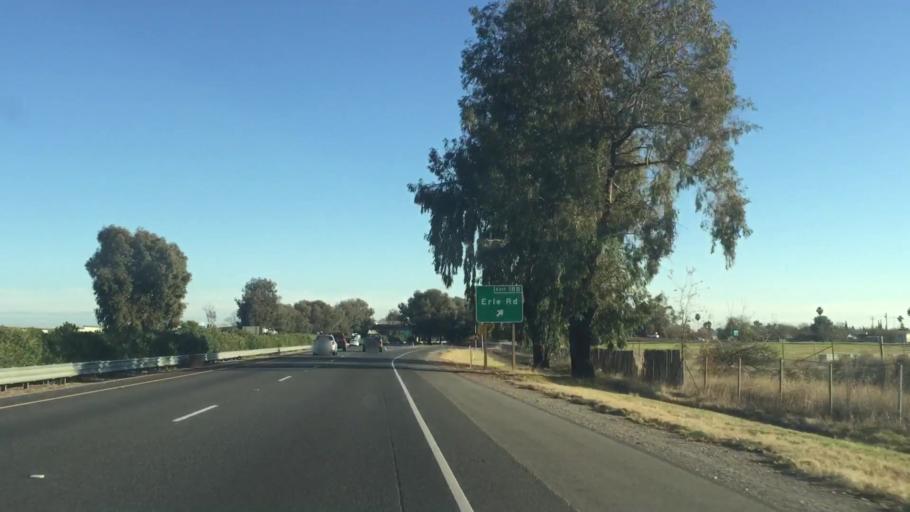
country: US
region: California
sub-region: Yuba County
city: Linda
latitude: 39.1158
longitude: -121.5631
